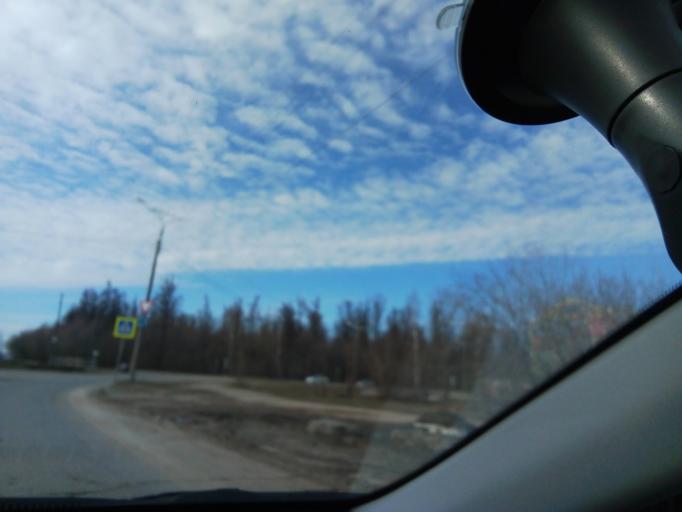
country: RU
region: Chuvashia
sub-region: Cheboksarskiy Rayon
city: Cheboksary
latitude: 56.0966
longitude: 47.2601
